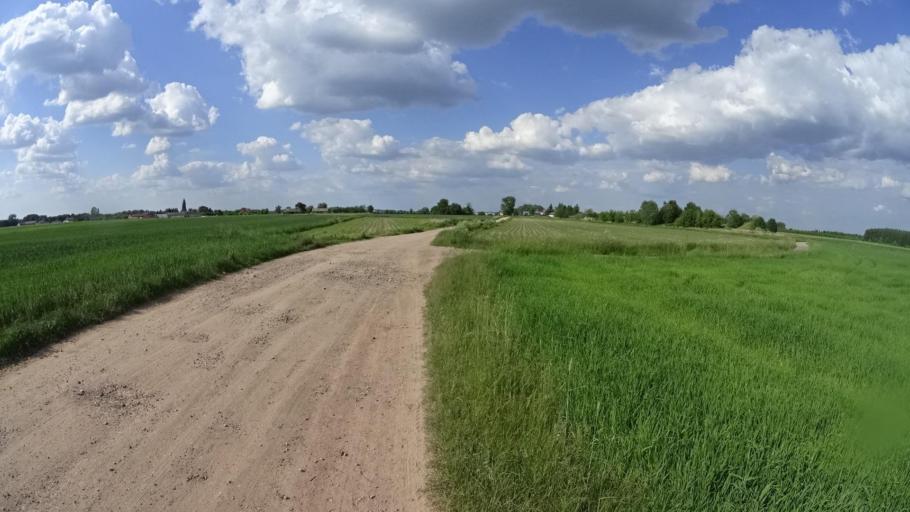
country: PL
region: Masovian Voivodeship
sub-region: Powiat piaseczynski
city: Tarczyn
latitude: 52.0253
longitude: 20.8178
